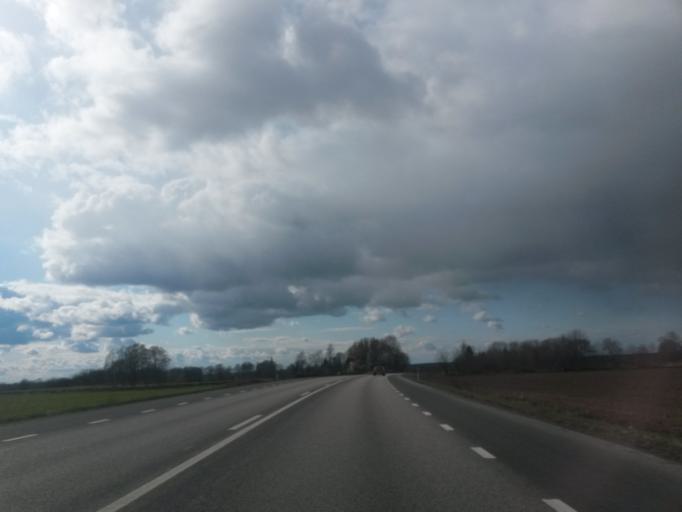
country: SE
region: Vaestra Goetaland
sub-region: Skara Kommun
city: Axvall
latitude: 58.3835
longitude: 13.6694
